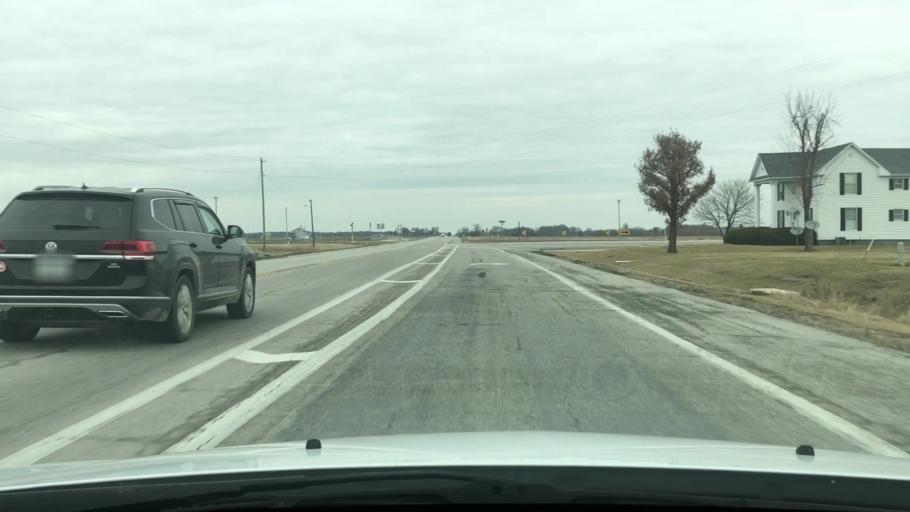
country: US
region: Missouri
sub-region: Audrain County
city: Vandalia
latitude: 39.2792
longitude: -91.6441
